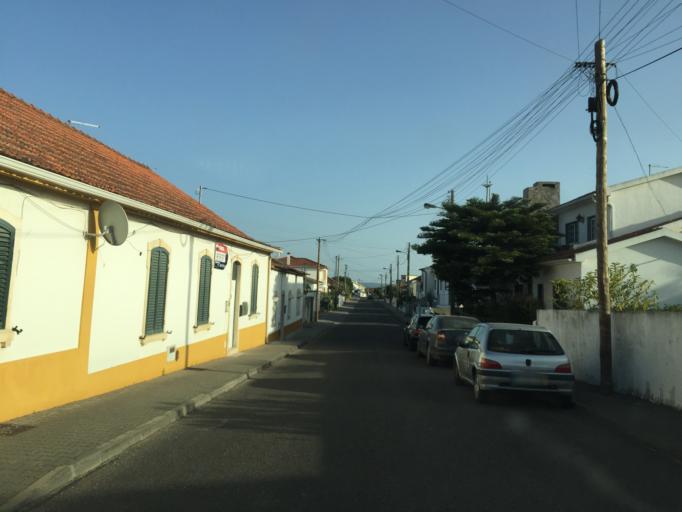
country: PT
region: Santarem
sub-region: Entroncamento
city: Entroncamento
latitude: 39.4796
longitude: -8.4521
